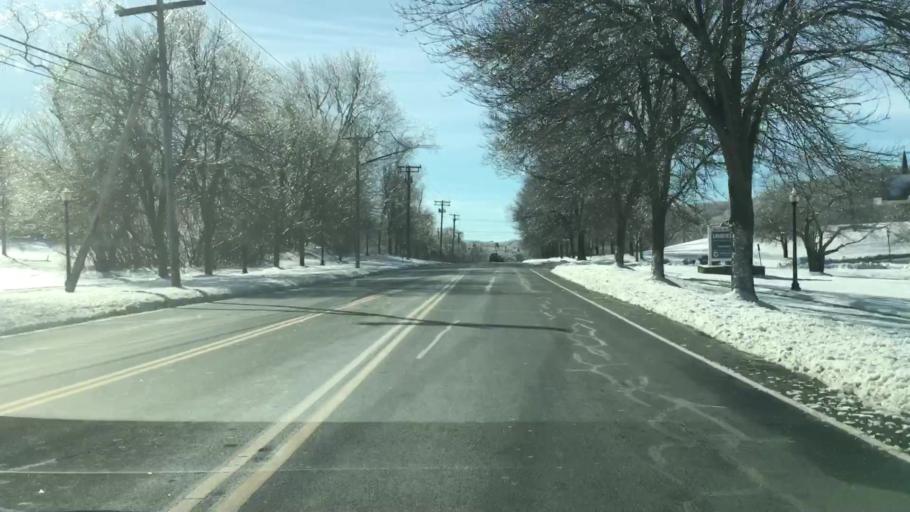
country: US
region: Connecticut
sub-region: New Haven County
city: Heritage Village
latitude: 41.4616
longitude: -73.2336
